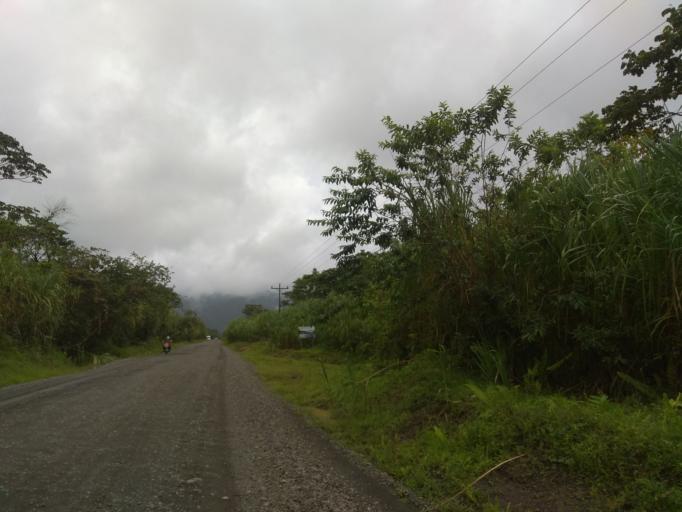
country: CR
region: Alajuela
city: La Fortuna
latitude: 10.4595
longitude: -84.7397
